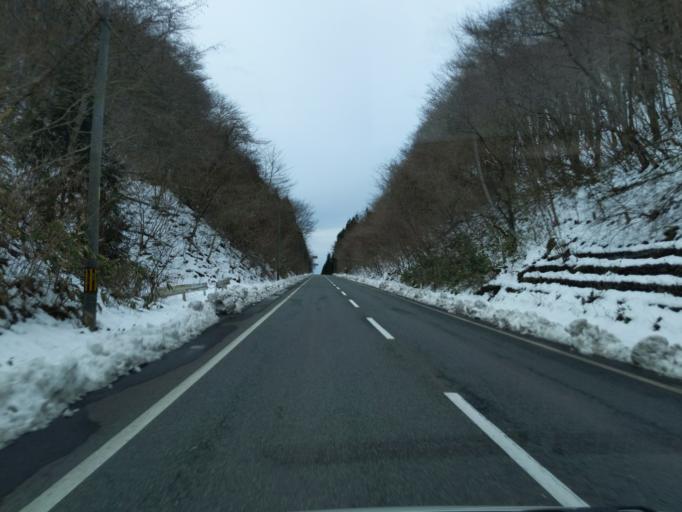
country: JP
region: Iwate
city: Mizusawa
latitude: 39.0924
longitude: 141.2710
